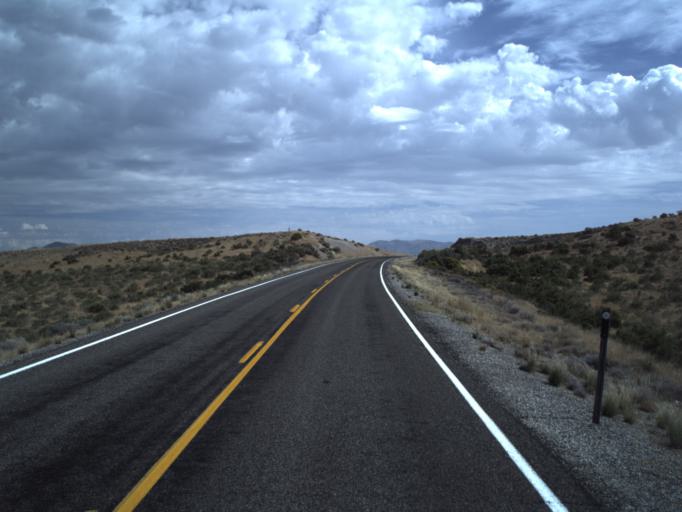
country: US
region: Utah
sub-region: Tooele County
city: Wendover
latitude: 41.4180
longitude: -113.9123
